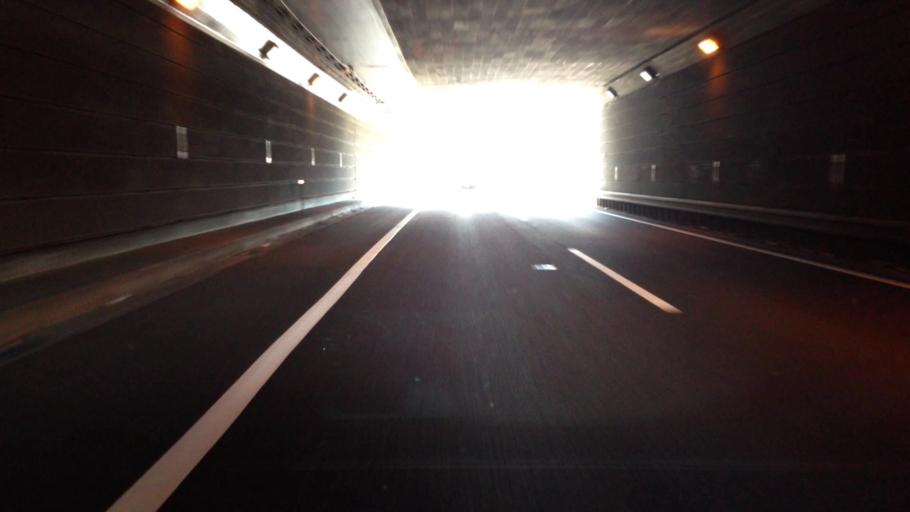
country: JP
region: Kanagawa
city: Yokohama
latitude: 35.4037
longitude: 139.5760
